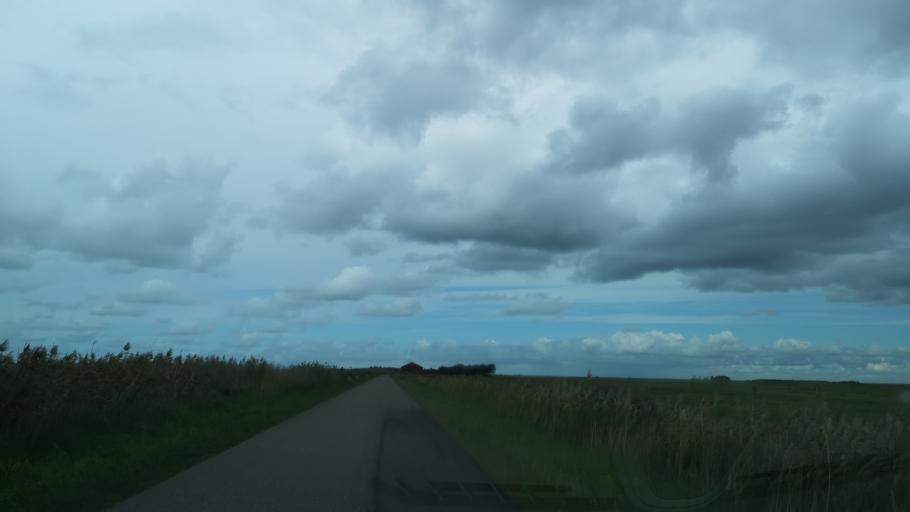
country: DK
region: Central Jutland
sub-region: Ringkobing-Skjern Kommune
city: Hvide Sande
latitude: 55.8380
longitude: 8.2175
